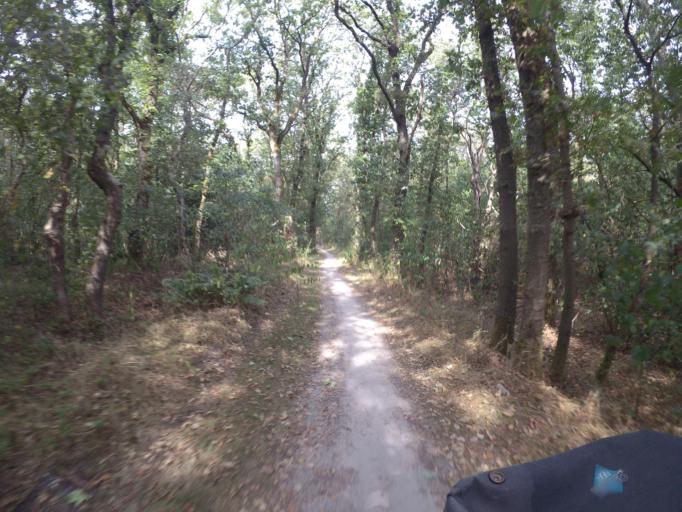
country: NL
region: Drenthe
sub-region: Gemeente Westerveld
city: Havelte
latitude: 52.8245
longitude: 6.2741
